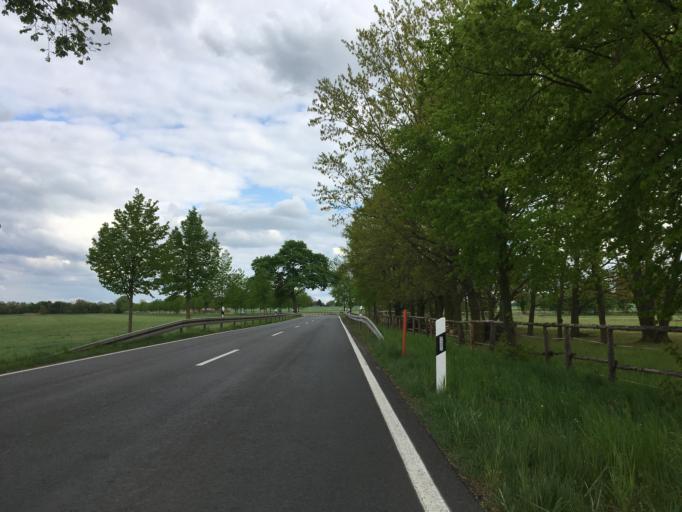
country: DE
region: Brandenburg
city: Bernau bei Berlin
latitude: 52.6631
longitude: 13.5903
